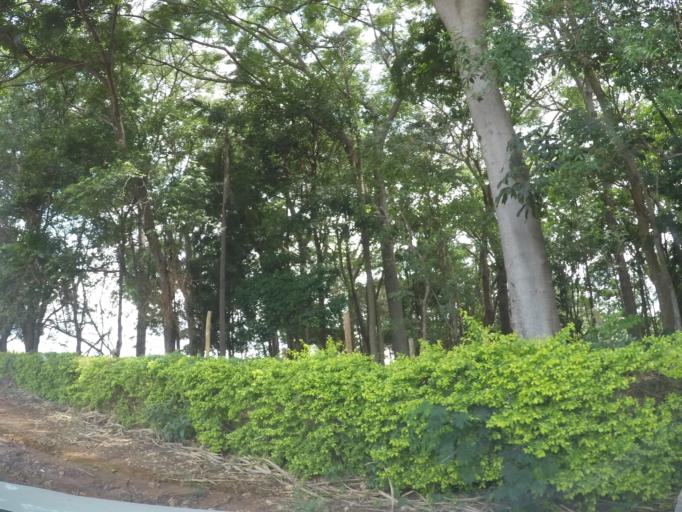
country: BR
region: Sao Paulo
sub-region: Sumare
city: Sumare
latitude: -22.8535
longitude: -47.3026
